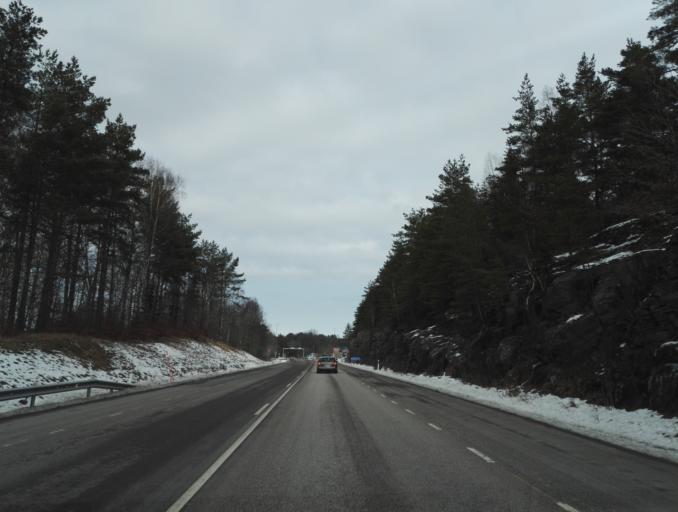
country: SE
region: Vaestra Goetaland
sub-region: Alingsas Kommun
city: Alingsas
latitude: 57.9106
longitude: 12.5551
